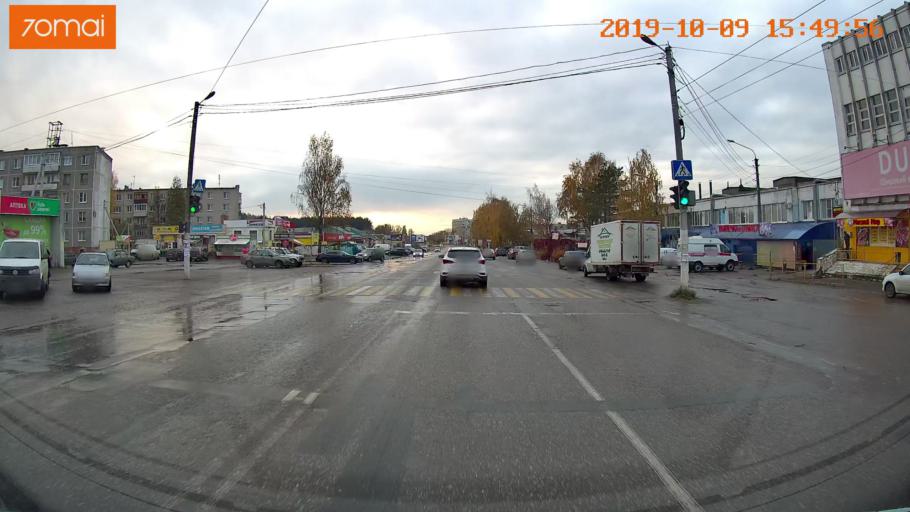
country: RU
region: Kostroma
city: Oktyabr'skiy
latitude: 57.8034
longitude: 40.9977
